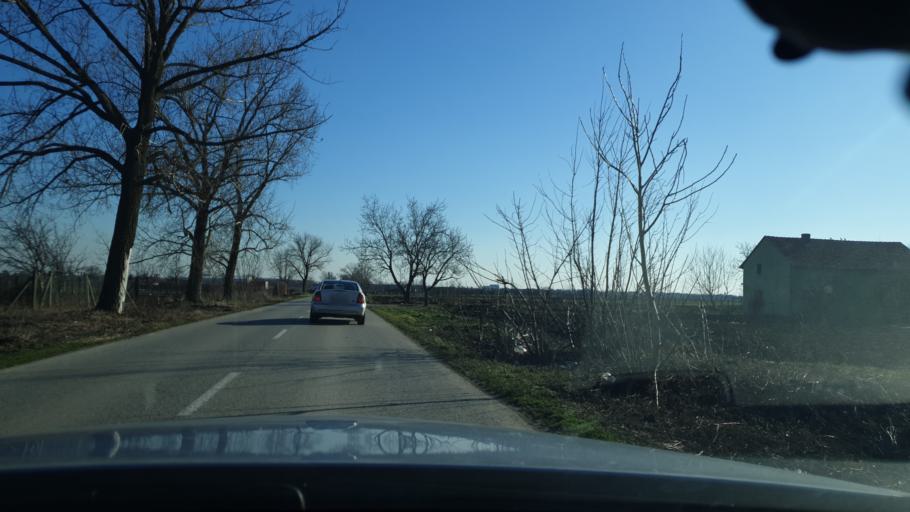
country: RS
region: Autonomna Pokrajina Vojvodina
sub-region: Sremski Okrug
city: Ruma
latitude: 45.0296
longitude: 19.8110
